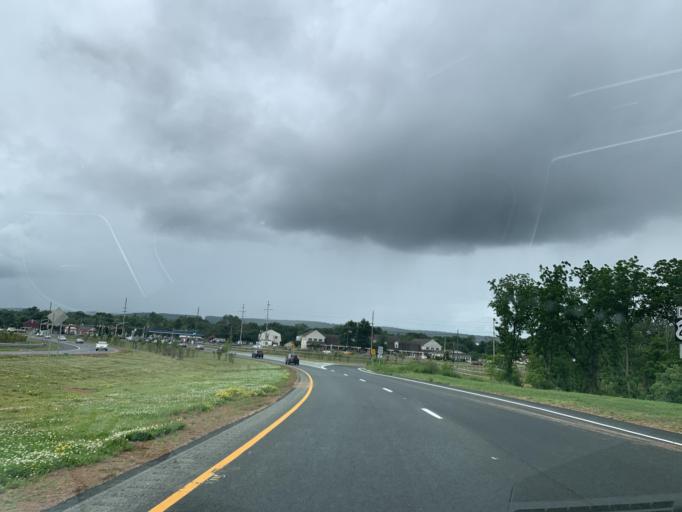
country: US
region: New Jersey
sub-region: Somerset County
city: Bloomingdale
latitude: 40.4793
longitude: -74.6521
